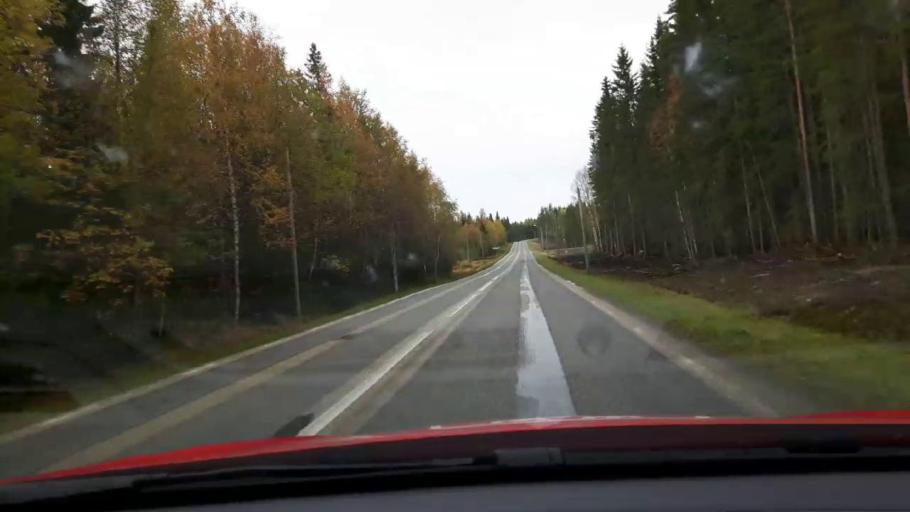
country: SE
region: Jaemtland
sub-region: Bergs Kommun
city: Hoverberg
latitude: 62.8176
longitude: 14.3999
